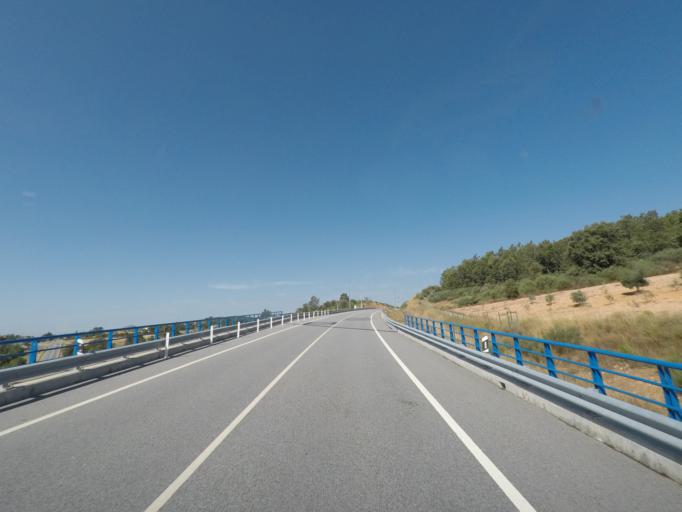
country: PT
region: Braganca
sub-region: Mogadouro
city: Mogadouro
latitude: 41.3449
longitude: -6.6293
